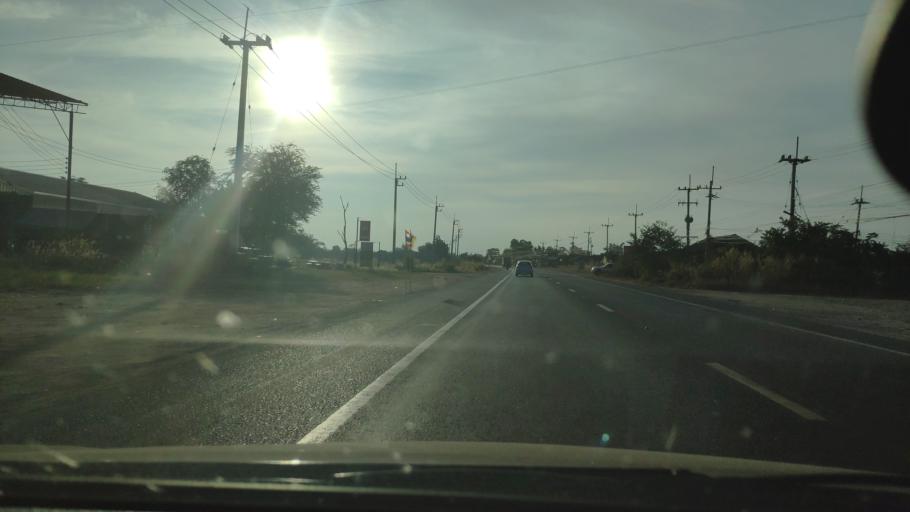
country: TH
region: Roi Et
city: Chiang Khwan
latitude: 16.1088
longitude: 103.8297
